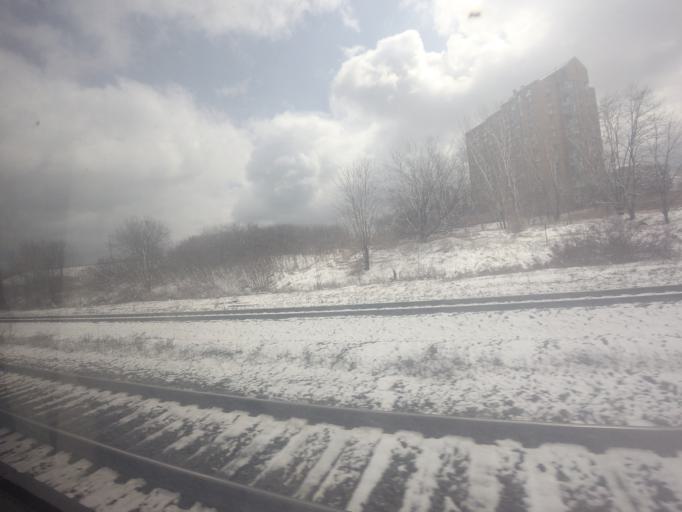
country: CA
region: Ontario
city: Scarborough
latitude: 43.7536
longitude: -79.2046
